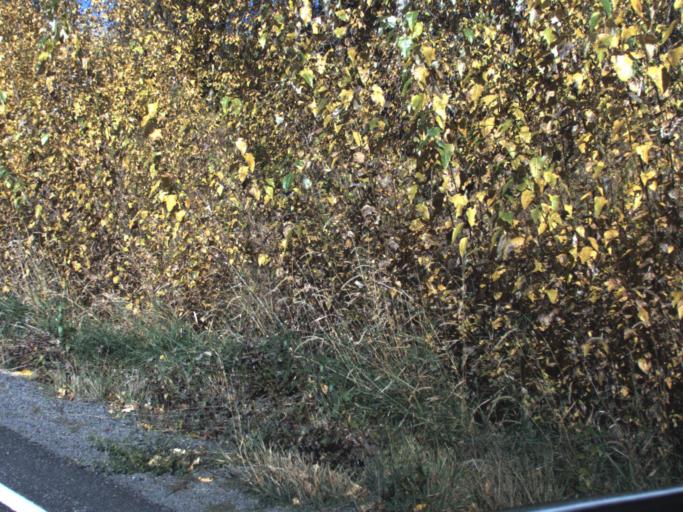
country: US
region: Washington
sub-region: Stevens County
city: Chewelah
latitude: 48.1574
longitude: -118.1666
